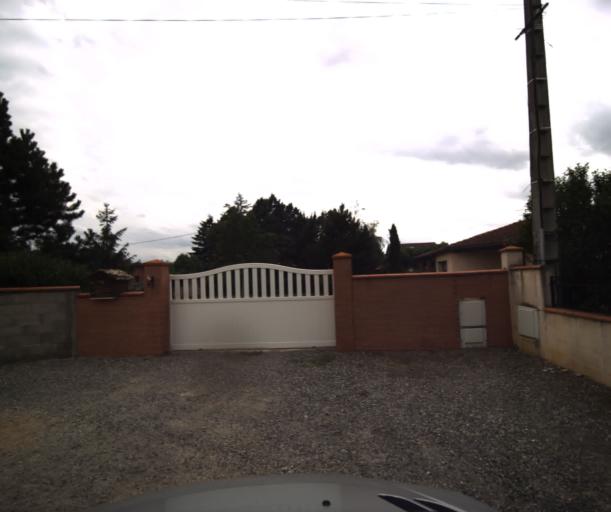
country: FR
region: Midi-Pyrenees
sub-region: Departement de la Haute-Garonne
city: Labarthe-sur-Leze
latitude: 43.4492
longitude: 1.3981
